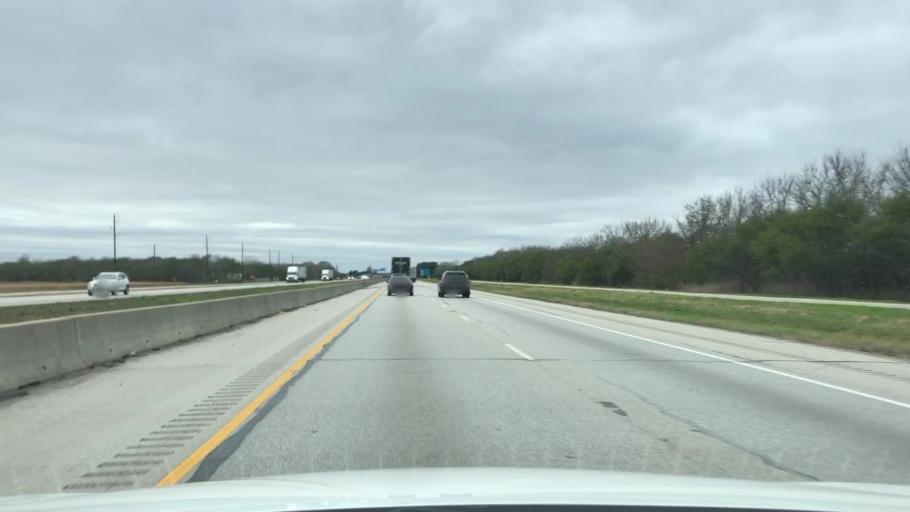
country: US
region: Texas
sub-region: Austin County
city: Sealy
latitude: 29.7756
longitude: -96.0902
